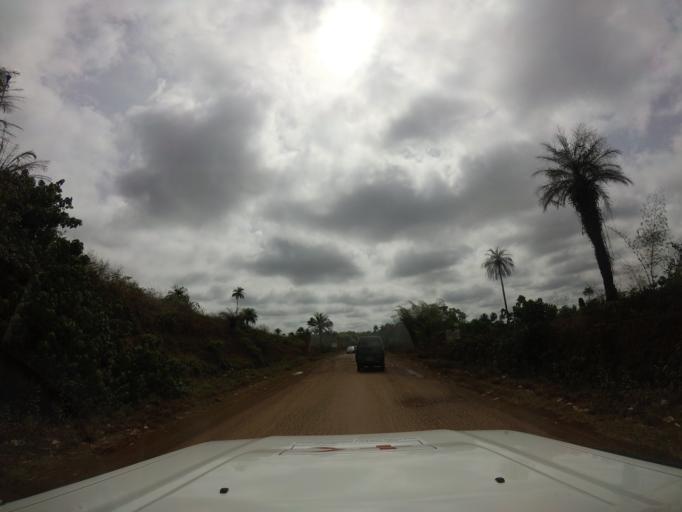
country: LR
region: Montserrado
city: Monrovia
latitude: 6.5235
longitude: -10.8351
